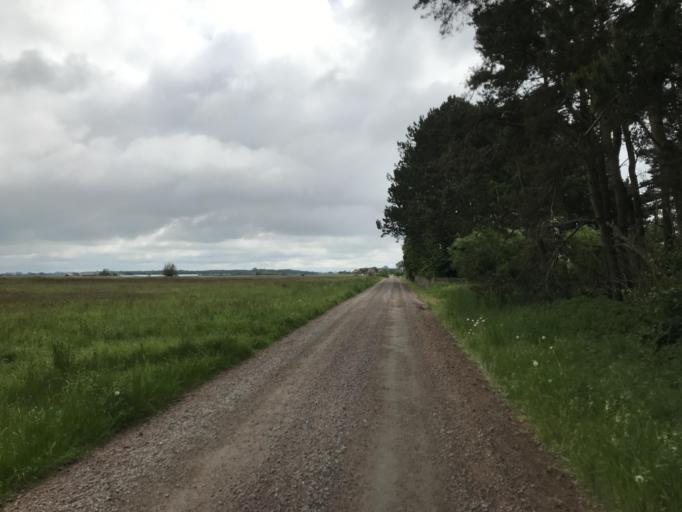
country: SE
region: Skane
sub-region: Landskrona
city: Asmundtorp
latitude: 55.8704
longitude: 12.9077
